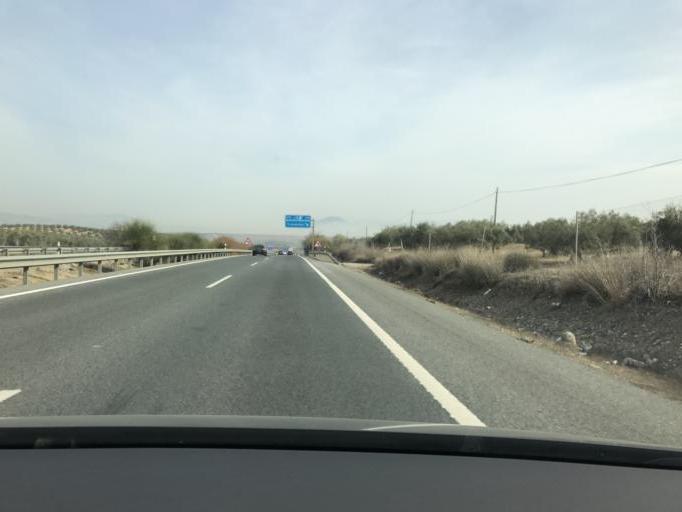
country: ES
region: Andalusia
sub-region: Provincia de Granada
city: Lachar
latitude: 37.1888
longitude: -3.8788
